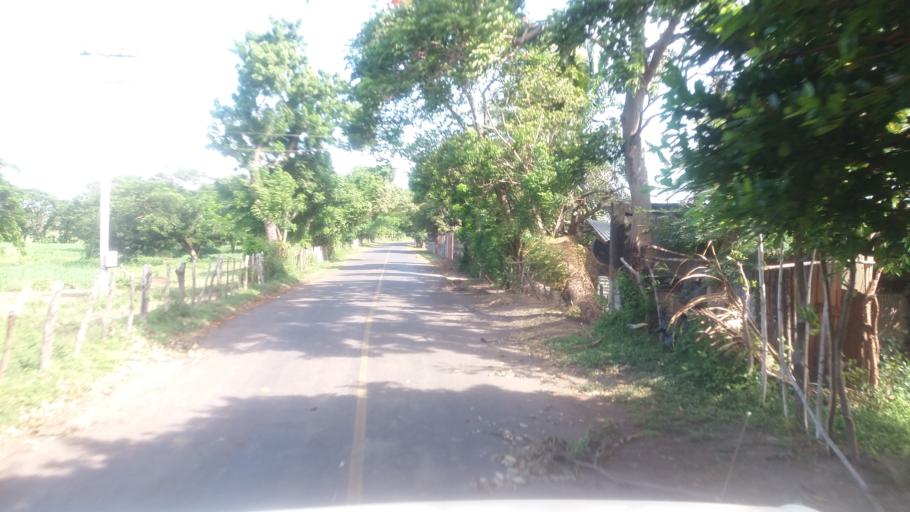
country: NI
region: Granada
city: Granada
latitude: 11.9599
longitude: -85.9450
